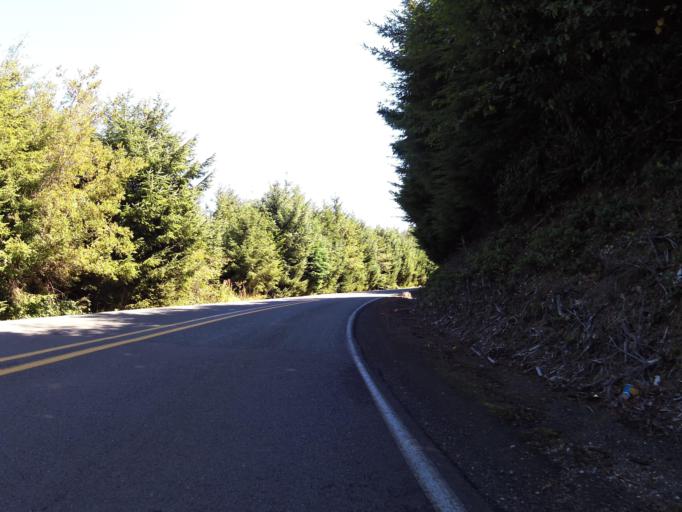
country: US
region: Oregon
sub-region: Coos County
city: Barview
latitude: 43.2712
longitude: -124.3490
